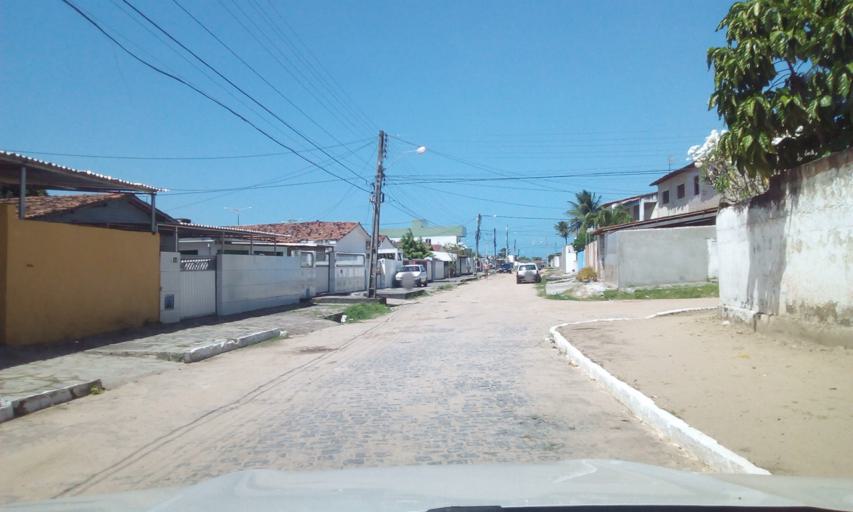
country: BR
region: Paraiba
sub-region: Joao Pessoa
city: Joao Pessoa
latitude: -7.1990
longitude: -34.8431
